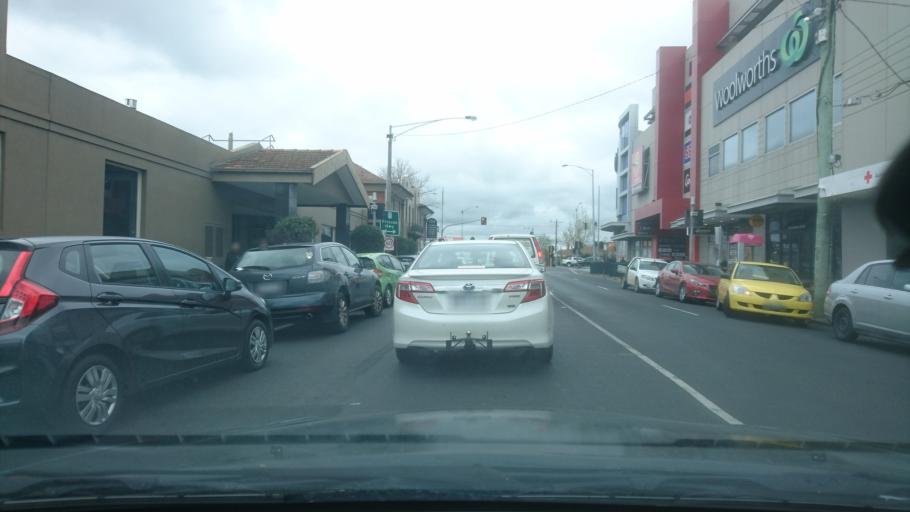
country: AU
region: Victoria
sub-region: Glen Eira
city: Carnegie
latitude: -37.8848
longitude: 145.0579
